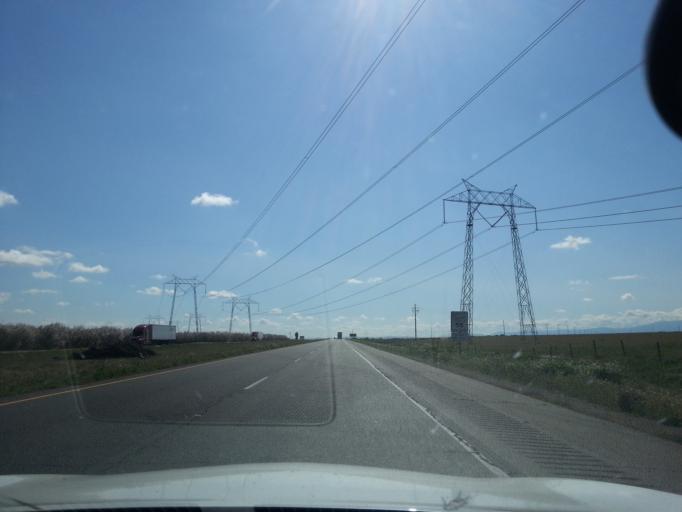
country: US
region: California
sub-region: Fresno County
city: Coalinga
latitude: 36.2883
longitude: -120.2657
